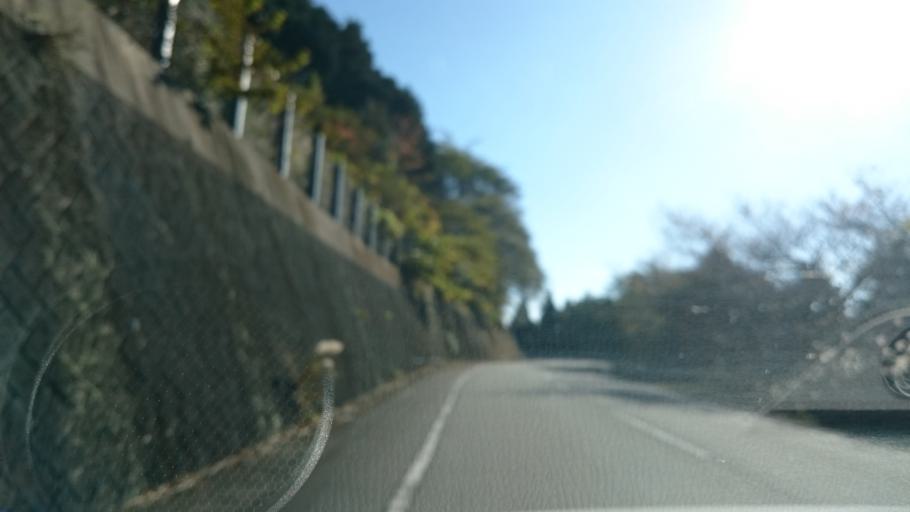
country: JP
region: Shizuoka
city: Heda
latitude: 34.9822
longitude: 138.8103
